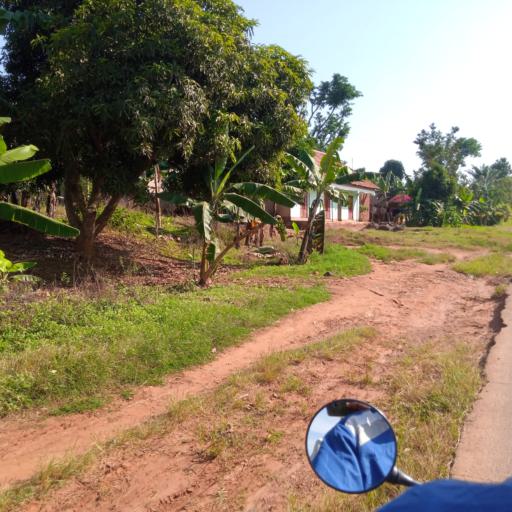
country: UG
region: Central Region
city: Masaka
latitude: -0.4530
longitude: 31.6675
